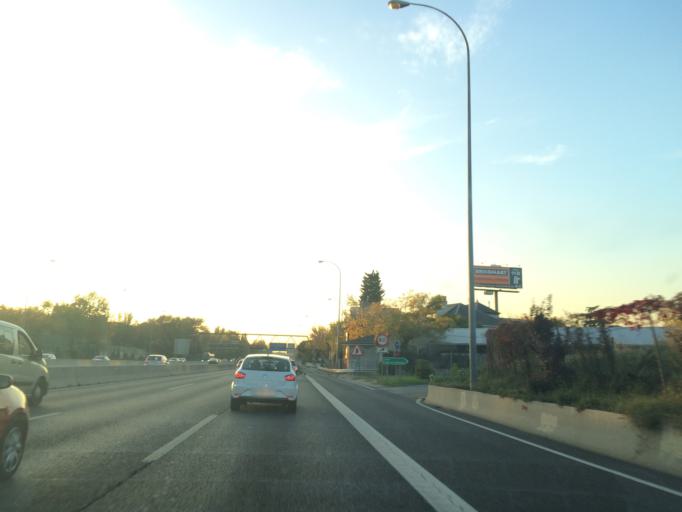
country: ES
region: Madrid
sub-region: Provincia de Madrid
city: Pozuelo de Alarcon
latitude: 40.4630
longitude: -3.7761
